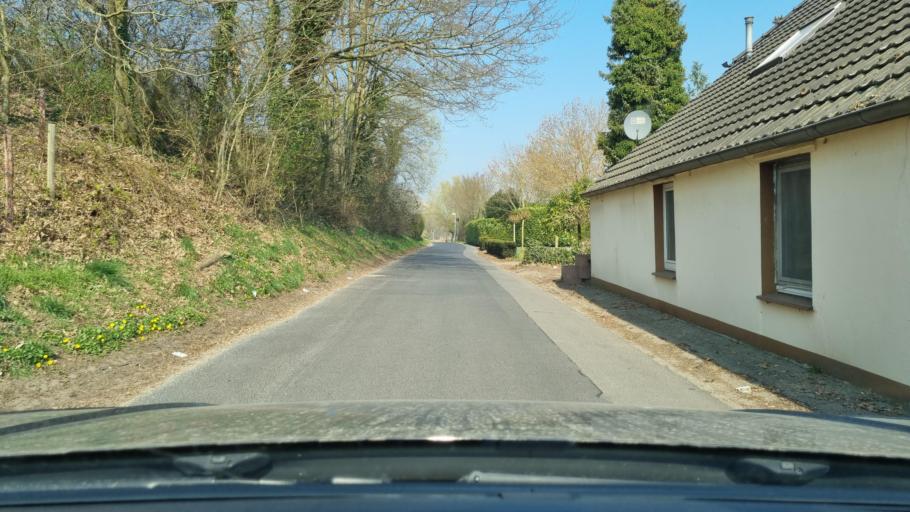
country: NL
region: Gelderland
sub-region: Gemeente Groesbeek
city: De Horst
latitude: 51.8062
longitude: 5.9699
